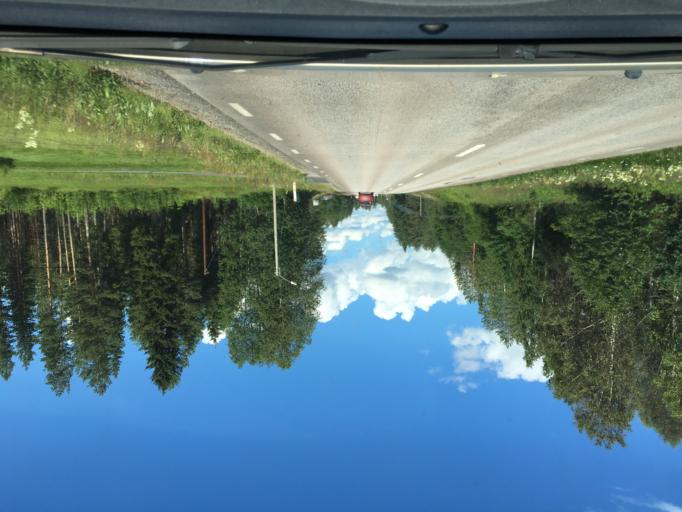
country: SE
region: Norrbotten
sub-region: Overkalix Kommun
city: OEverkalix
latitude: 66.2897
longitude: 22.8170
